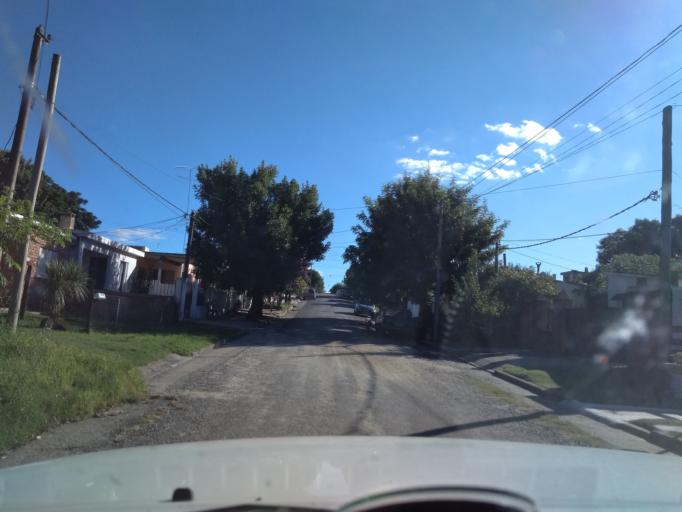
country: UY
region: Florida
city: Florida
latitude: -34.0931
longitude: -56.2080
